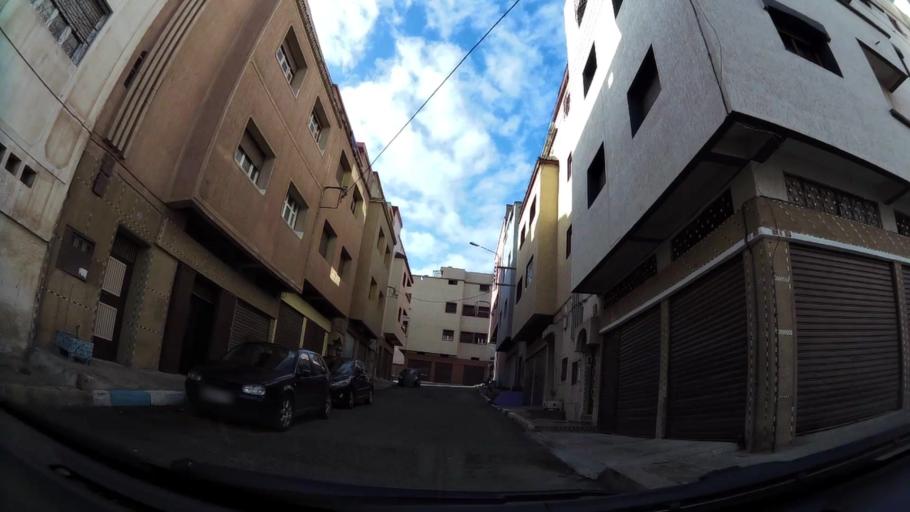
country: MA
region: Grand Casablanca
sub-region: Casablanca
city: Casablanca
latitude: 33.5424
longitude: -7.5930
